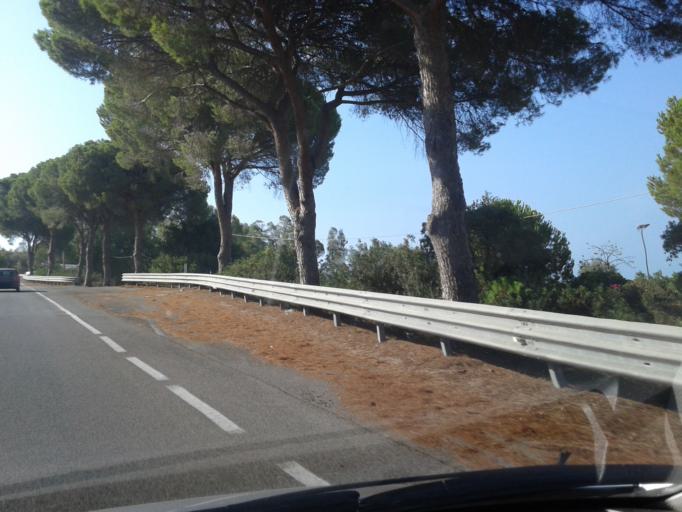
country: IT
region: Sicily
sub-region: Palermo
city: Finale
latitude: 38.0237
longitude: 14.1500
